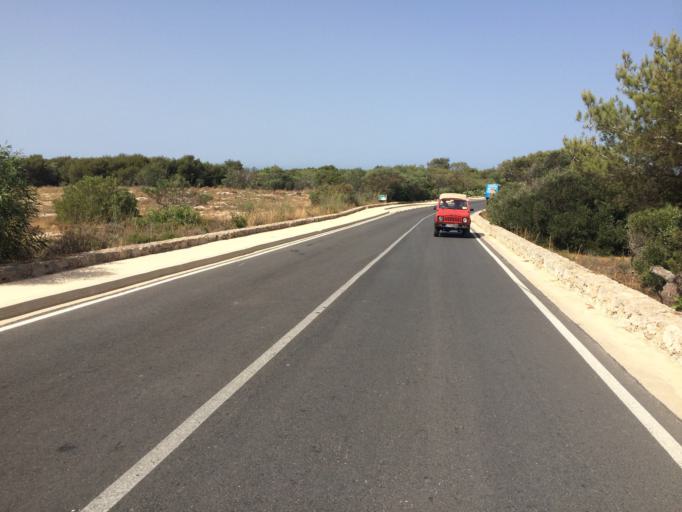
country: MT
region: Il-Mellieha
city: Mellieha
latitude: 35.9820
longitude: 14.3590
